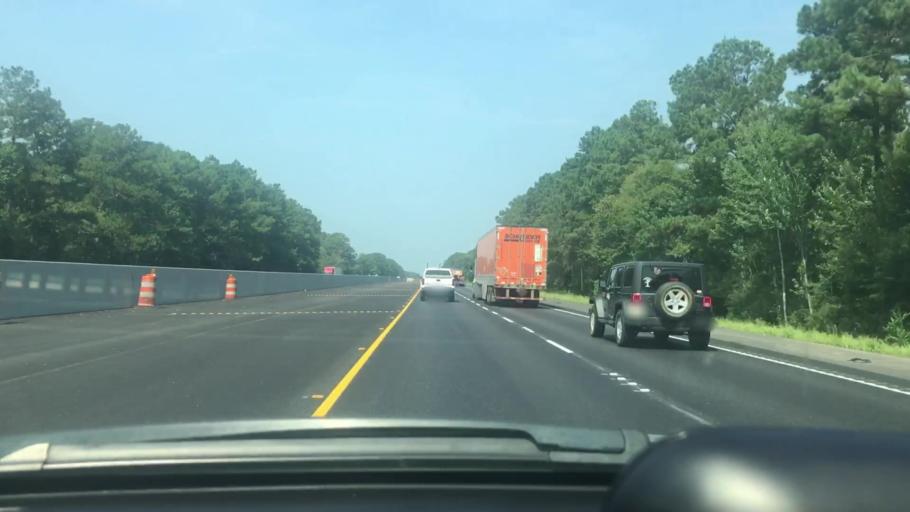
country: US
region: Louisiana
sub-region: Livingston Parish
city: Livingston
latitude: 30.4748
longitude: -90.6699
